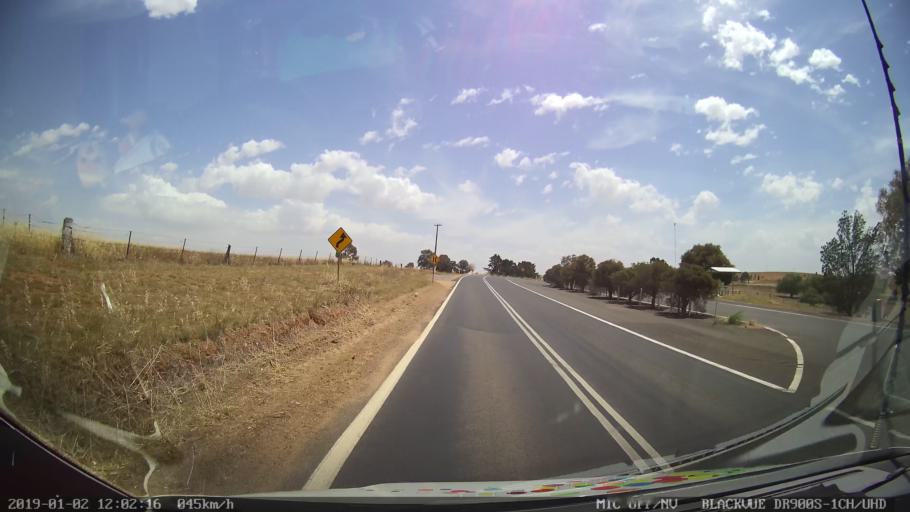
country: AU
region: New South Wales
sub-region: Young
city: Young
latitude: -34.5395
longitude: 148.3245
